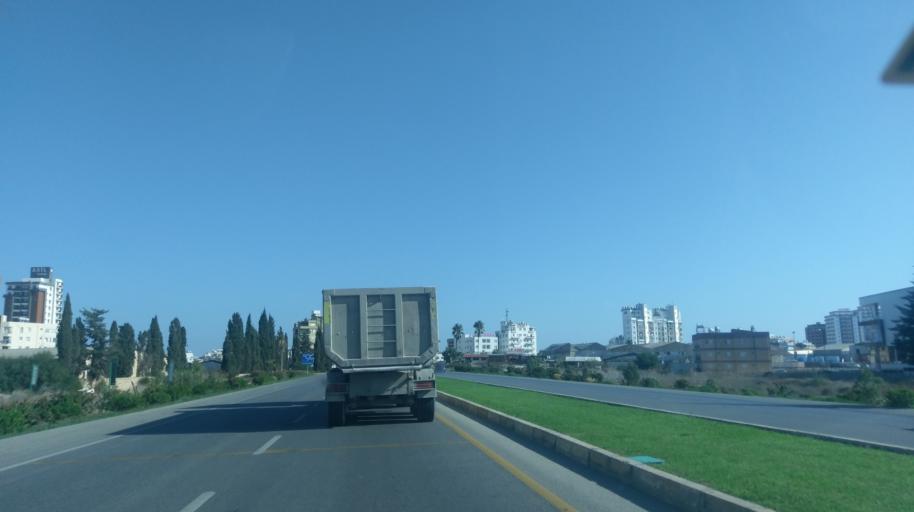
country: CY
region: Ammochostos
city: Famagusta
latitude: 35.1264
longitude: 33.9191
